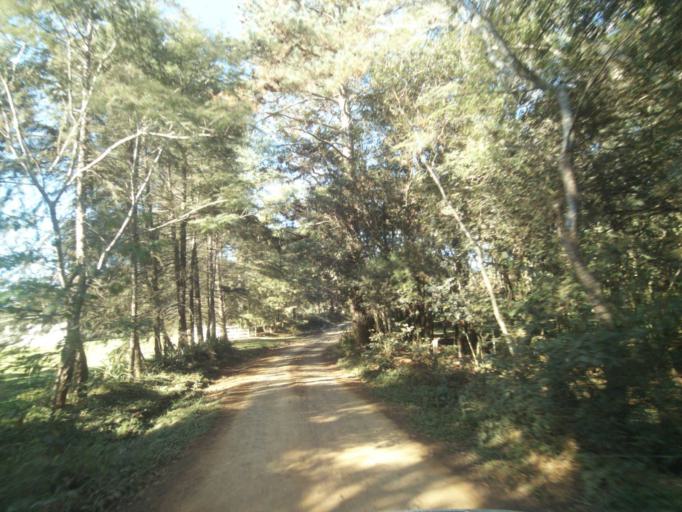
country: BR
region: Parana
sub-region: Tibagi
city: Tibagi
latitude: -24.5514
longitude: -50.5193
